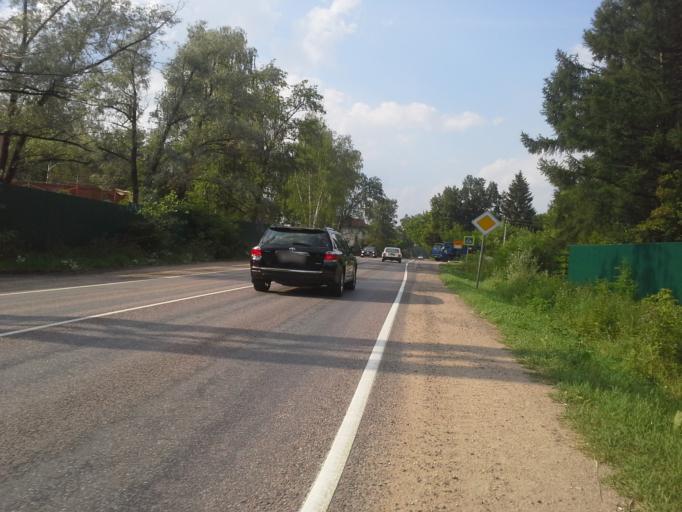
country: RU
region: Moskovskaya
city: Istra
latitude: 55.8873
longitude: 36.7977
